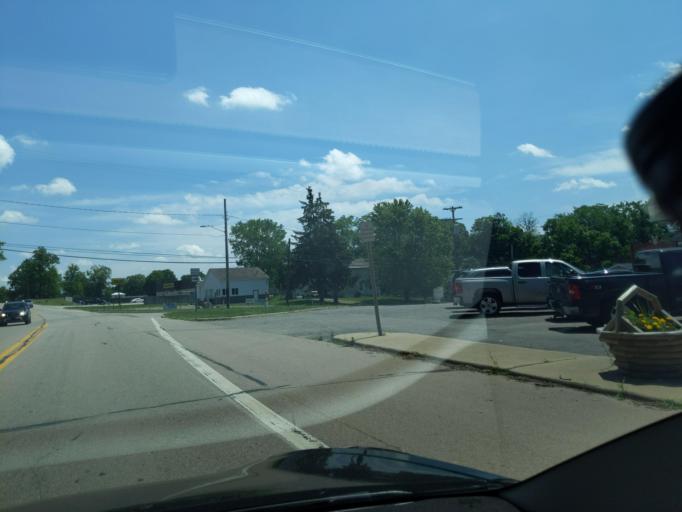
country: US
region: Michigan
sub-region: Ionia County
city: Ionia
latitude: 43.0015
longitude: -84.9450
